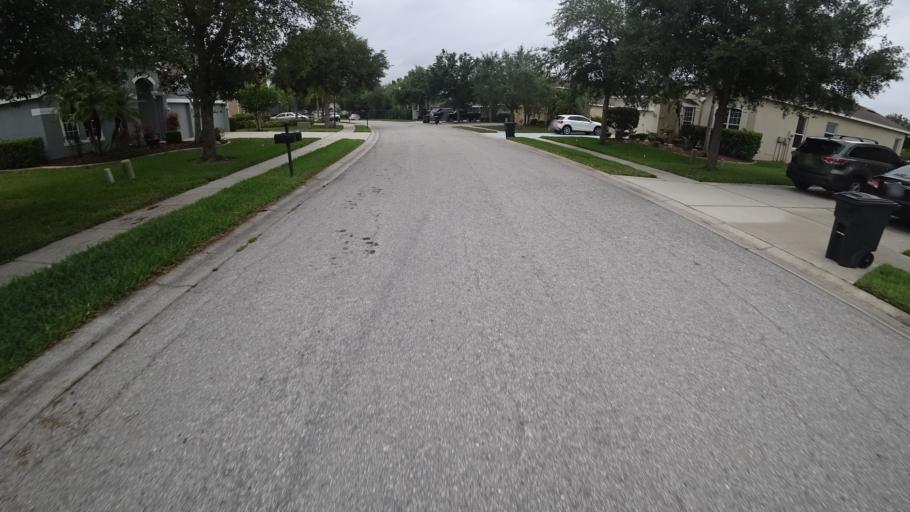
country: US
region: Florida
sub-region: Manatee County
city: Samoset
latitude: 27.4337
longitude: -82.5092
